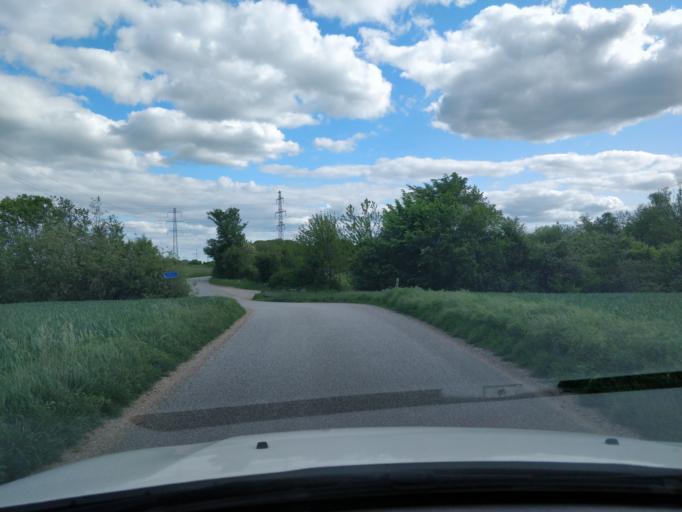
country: DK
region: Capital Region
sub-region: Hoje-Taastrup Kommune
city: Flong
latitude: 55.6814
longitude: 12.2195
